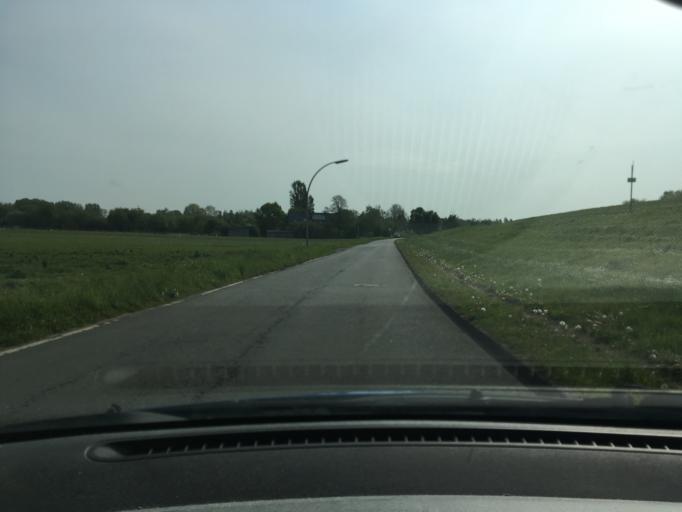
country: DE
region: Hamburg
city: Harburg
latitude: 53.4789
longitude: 10.0297
